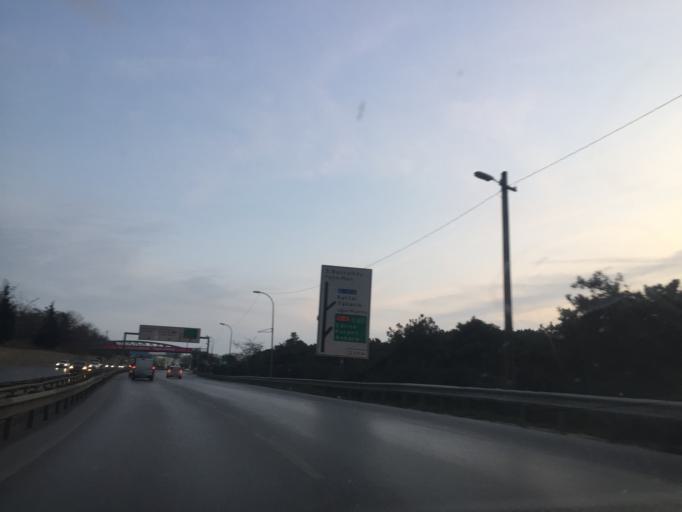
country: TR
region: Istanbul
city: Samandira
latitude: 40.9734
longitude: 29.2190
